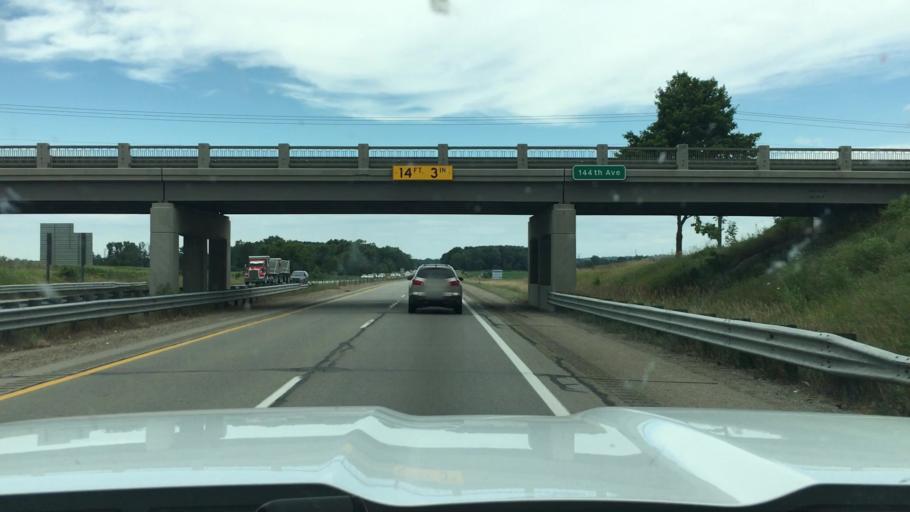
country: US
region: Michigan
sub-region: Allegan County
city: Wayland
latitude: 42.7391
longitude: -85.6732
